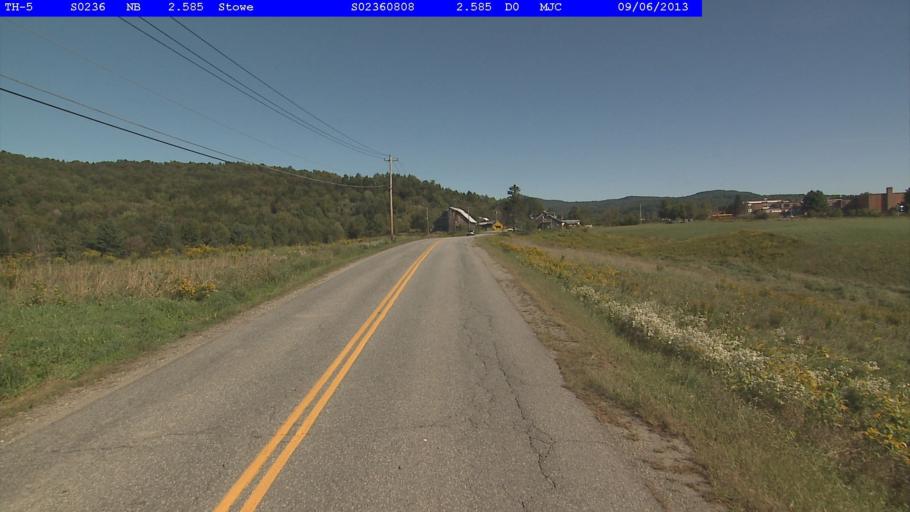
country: US
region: Vermont
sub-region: Washington County
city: Waterbury
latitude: 44.4620
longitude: -72.7290
